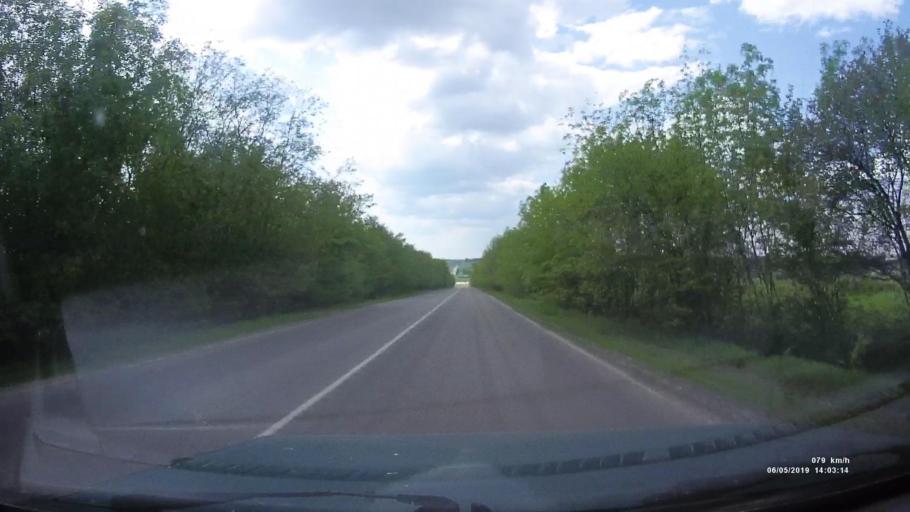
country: RU
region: Rostov
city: Shakhty
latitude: 47.6811
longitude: 40.3500
